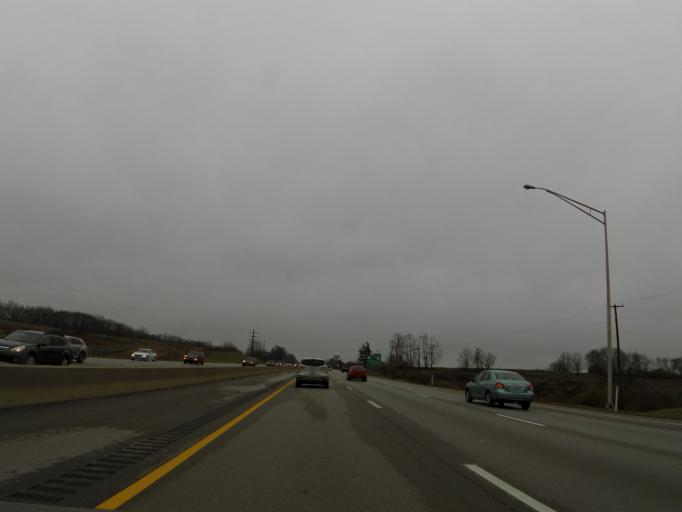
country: US
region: Kentucky
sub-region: Scott County
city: Georgetown
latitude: 38.2438
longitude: -84.5457
